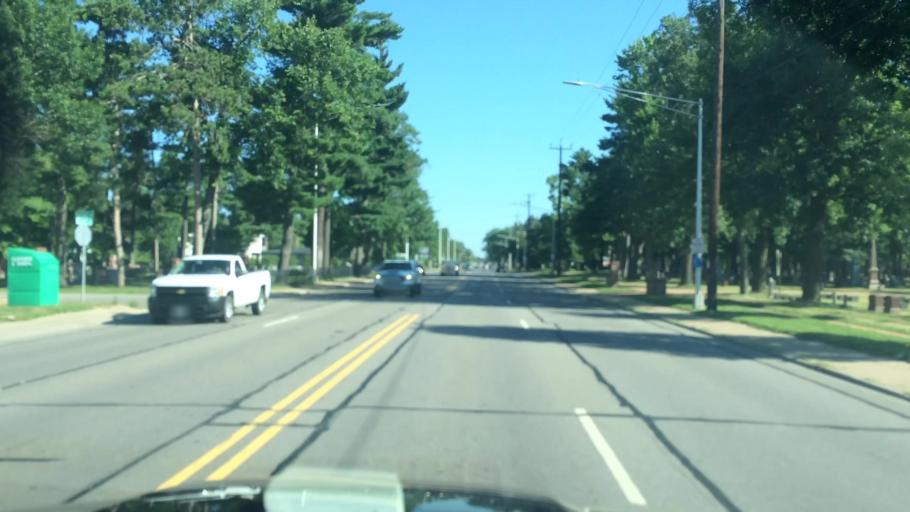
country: US
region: Wisconsin
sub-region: Marathon County
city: Wausau
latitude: 44.9398
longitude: -89.6186
